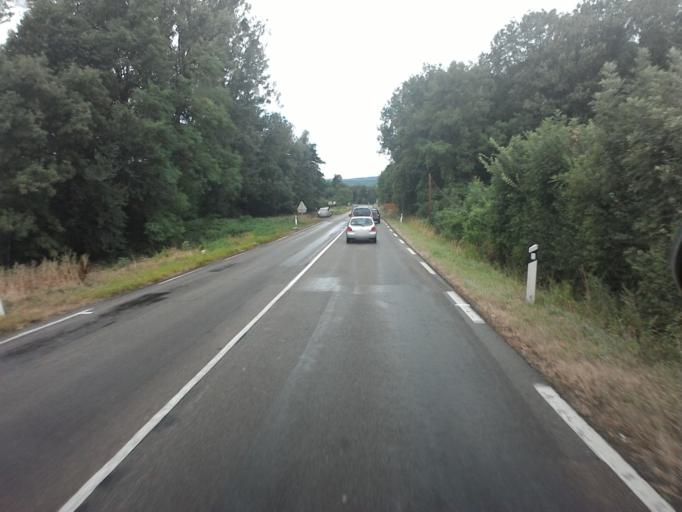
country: FR
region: Franche-Comte
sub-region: Departement du Jura
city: Poligny
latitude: 46.8505
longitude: 5.7092
